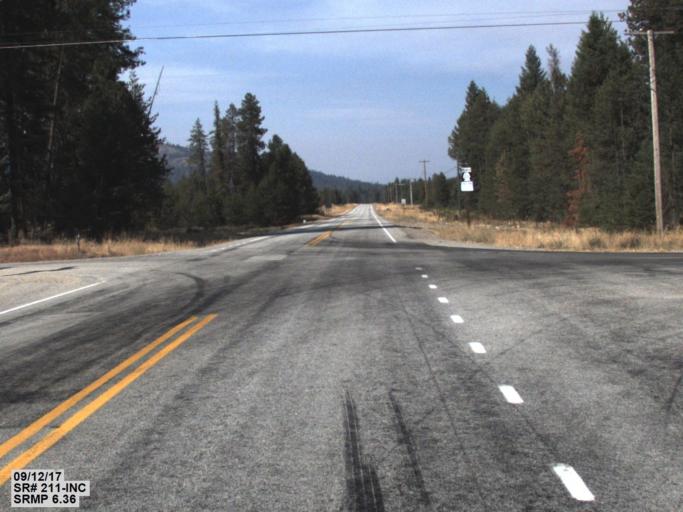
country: US
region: Washington
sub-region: Pend Oreille County
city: Newport
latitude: 48.1813
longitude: -117.3015
